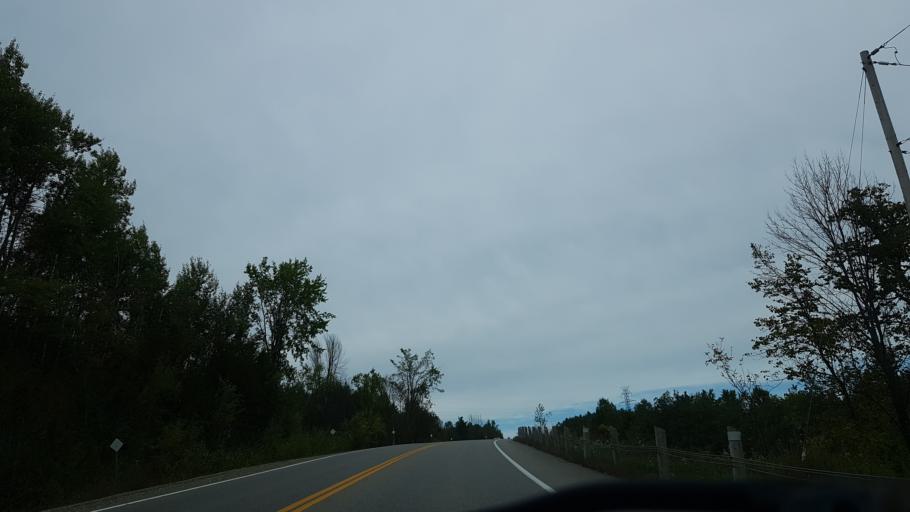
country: CA
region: Ontario
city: Orangeville
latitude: 44.0742
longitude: -80.0171
